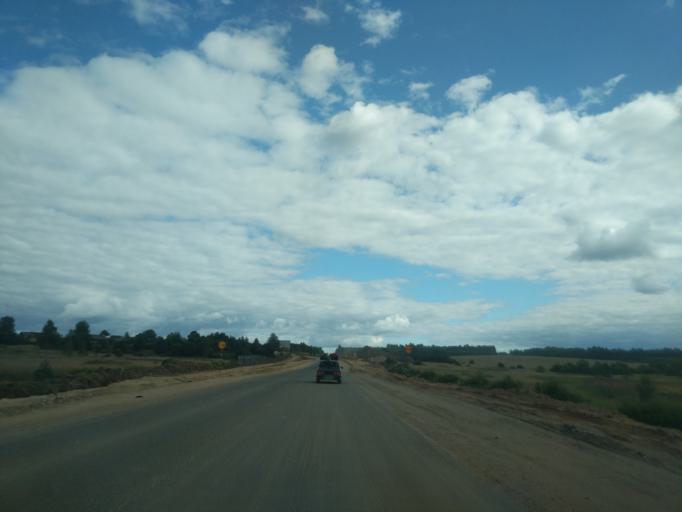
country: RU
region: Kostroma
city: Sudislavl'
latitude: 57.8758
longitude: 41.7321
